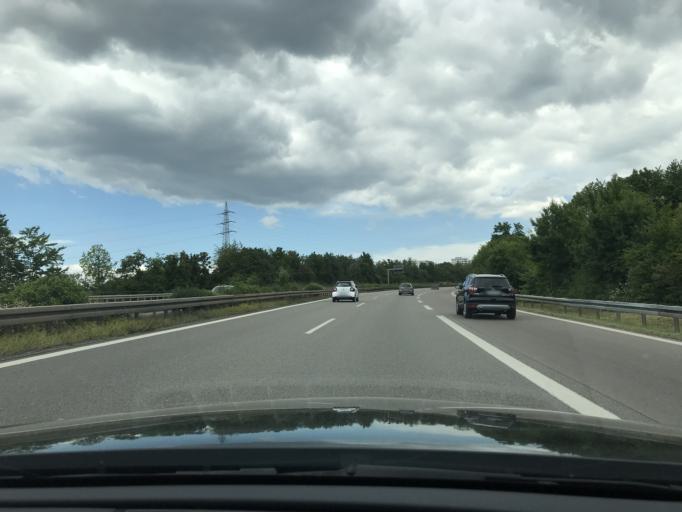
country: DE
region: Baden-Wuerttemberg
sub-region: Regierungsbezirk Stuttgart
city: Waiblingen
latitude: 48.8287
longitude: 9.3330
